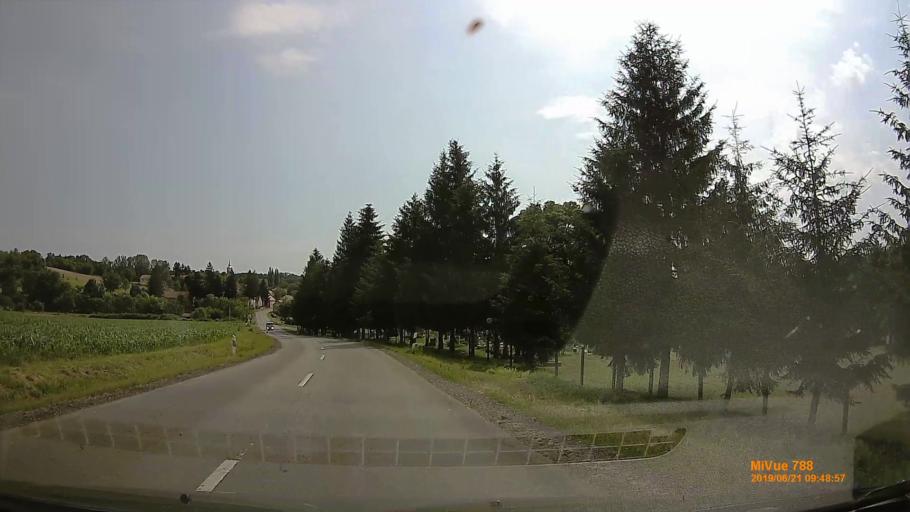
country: HU
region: Baranya
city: Sasd
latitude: 46.2682
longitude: 18.0361
